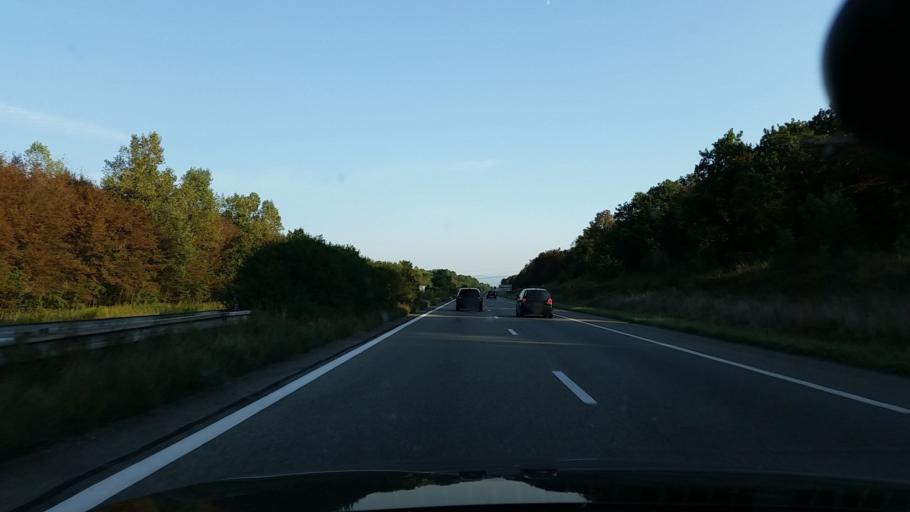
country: FR
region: Alsace
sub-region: Departement du Haut-Rhin
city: Bartenheim
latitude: 47.6521
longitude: 7.4905
